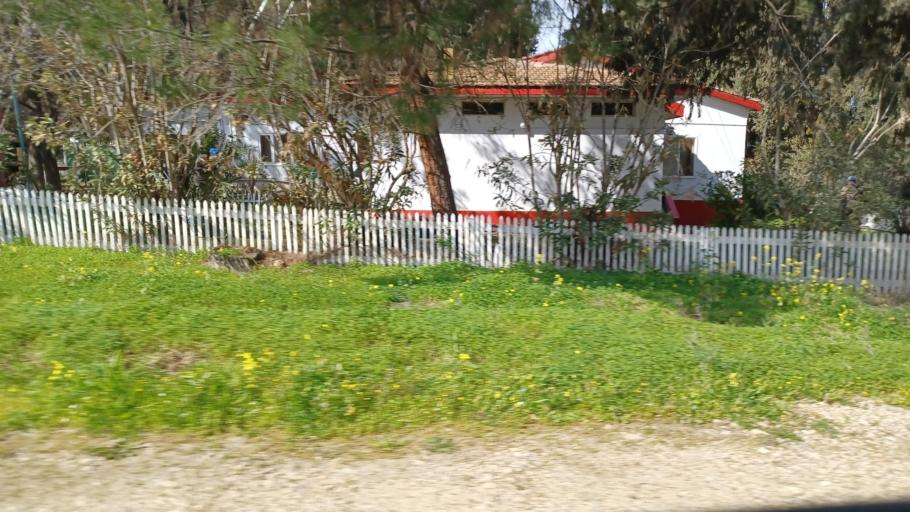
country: CY
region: Lefkosia
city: Lefka
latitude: 35.0912
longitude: 32.8870
